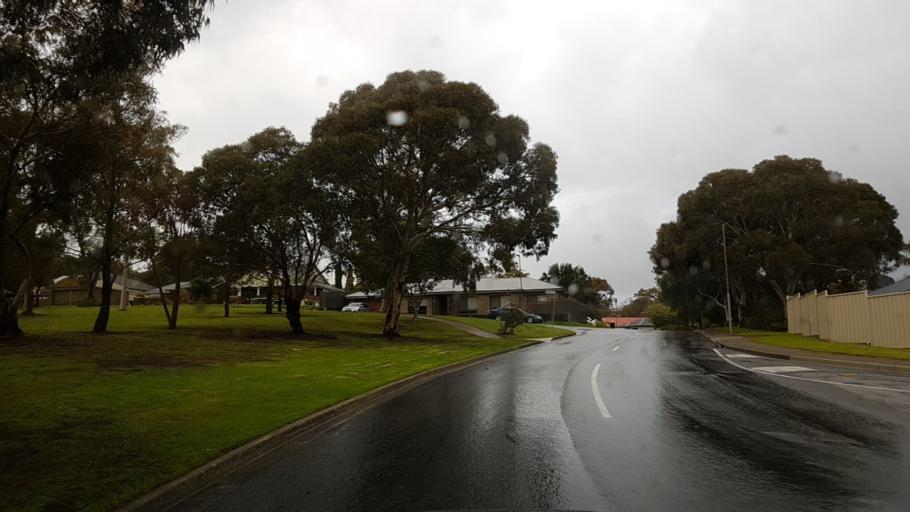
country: AU
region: South Australia
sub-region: Onkaparinga
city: Craigburn Farm
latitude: -35.0813
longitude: 138.5916
